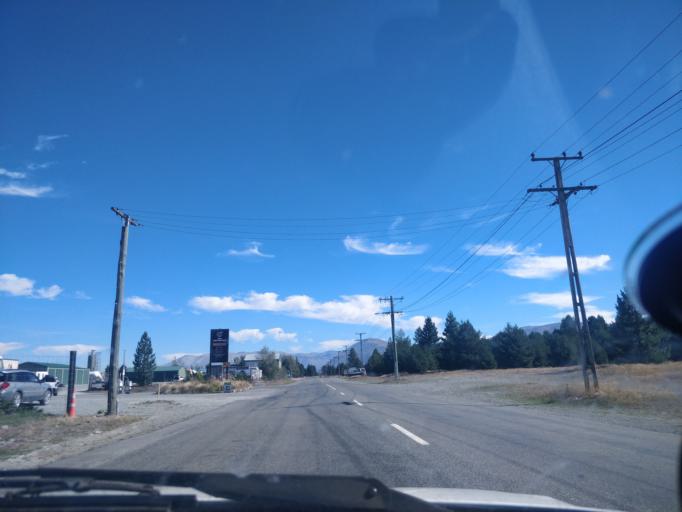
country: NZ
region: Otago
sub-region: Queenstown-Lakes District
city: Wanaka
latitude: -44.2646
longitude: 170.0902
